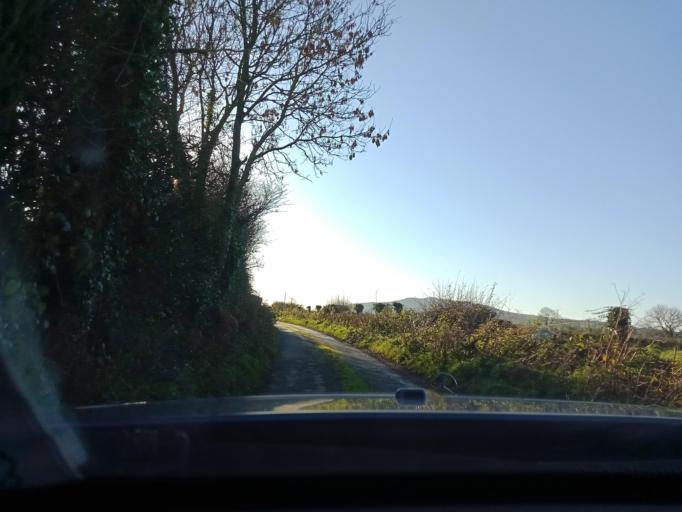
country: IE
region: Munster
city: Carrick-on-Suir
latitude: 52.4367
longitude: -7.3933
